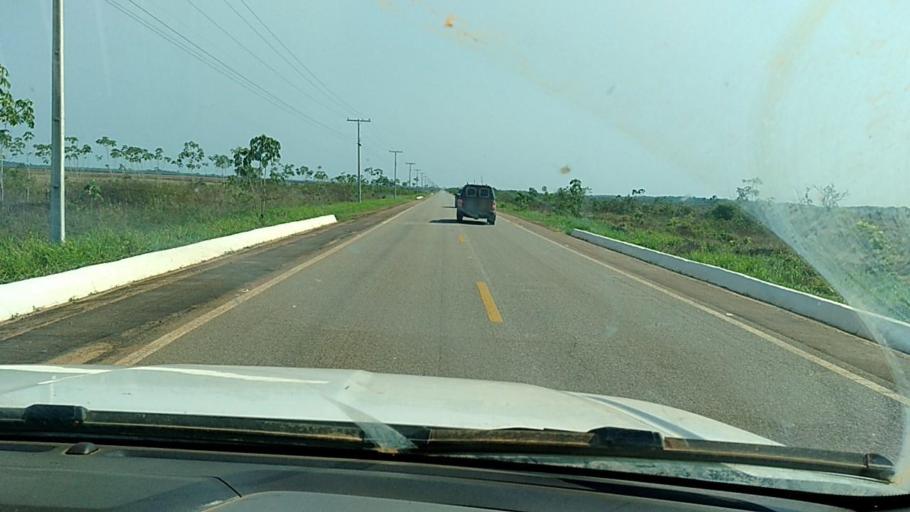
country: BR
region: Amazonas
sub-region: Humaita
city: Humaita
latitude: -7.6041
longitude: -63.0799
